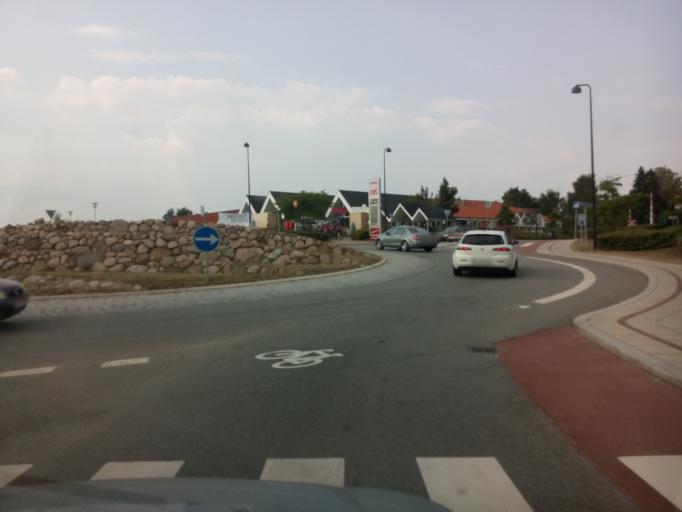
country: DK
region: Central Jutland
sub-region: Skanderborg Kommune
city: Ry
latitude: 56.0925
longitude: 9.7554
